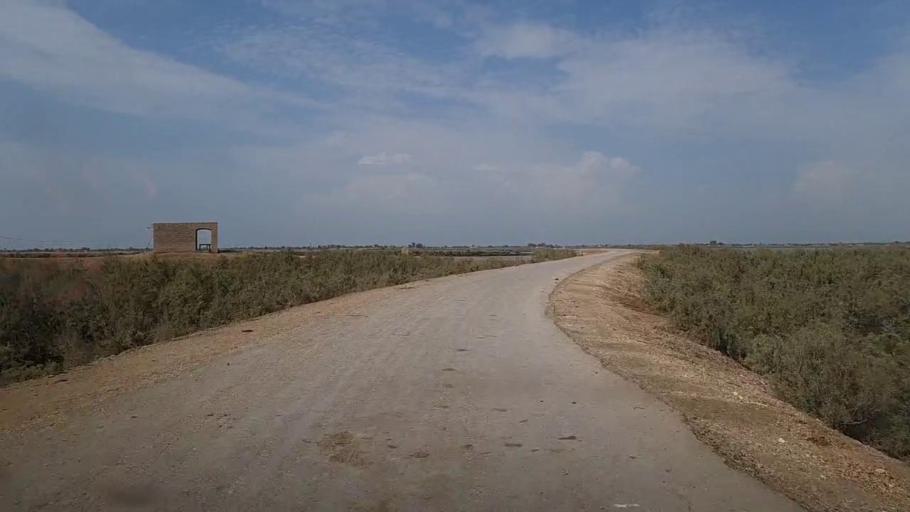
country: PK
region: Sindh
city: Thul
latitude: 28.2769
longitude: 68.8212
